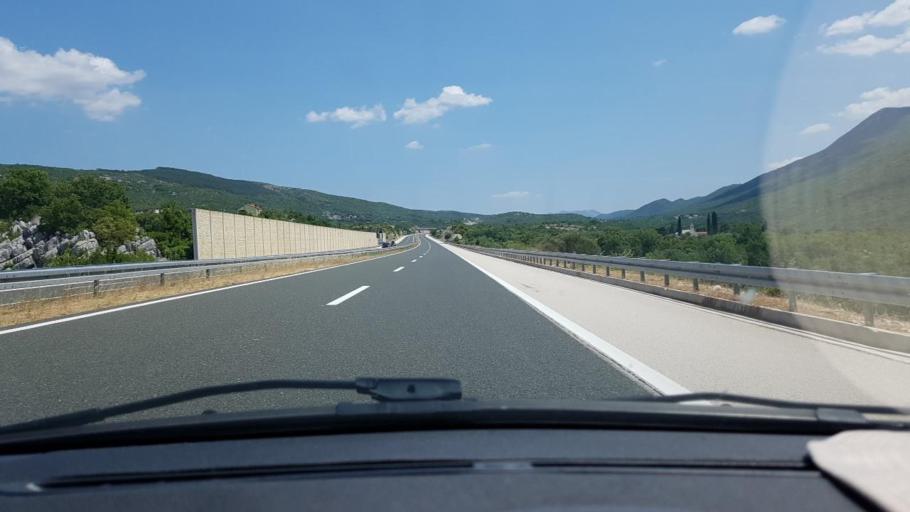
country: HR
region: Splitsko-Dalmatinska
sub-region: Grad Makarska
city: Makarska
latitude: 43.3917
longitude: 17.0508
